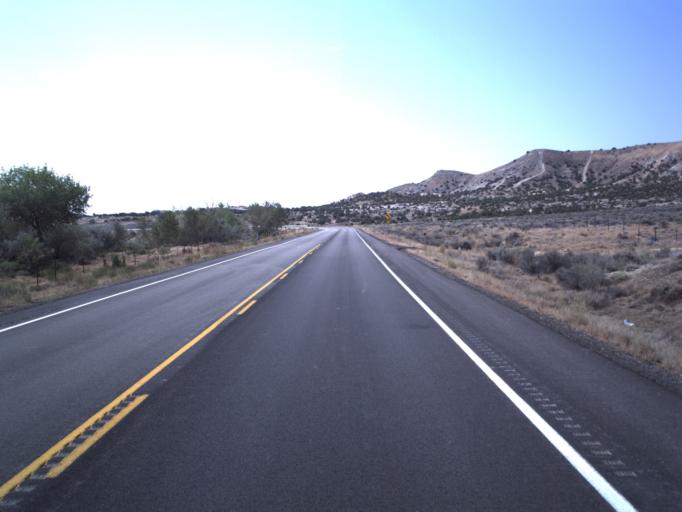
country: US
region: Utah
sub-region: Uintah County
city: Naples
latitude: 40.3605
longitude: -109.4982
